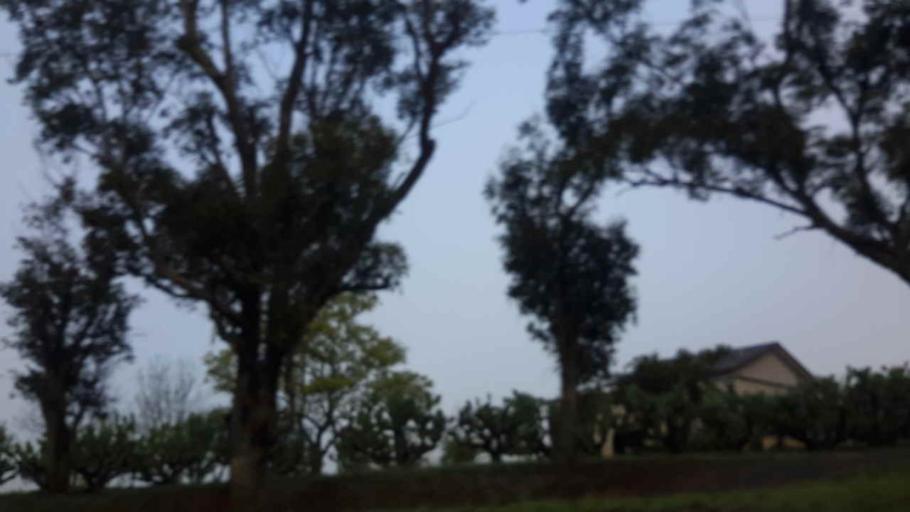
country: AU
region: New South Wales
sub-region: Liverpool
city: Luddenham
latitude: -33.8480
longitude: 150.6884
